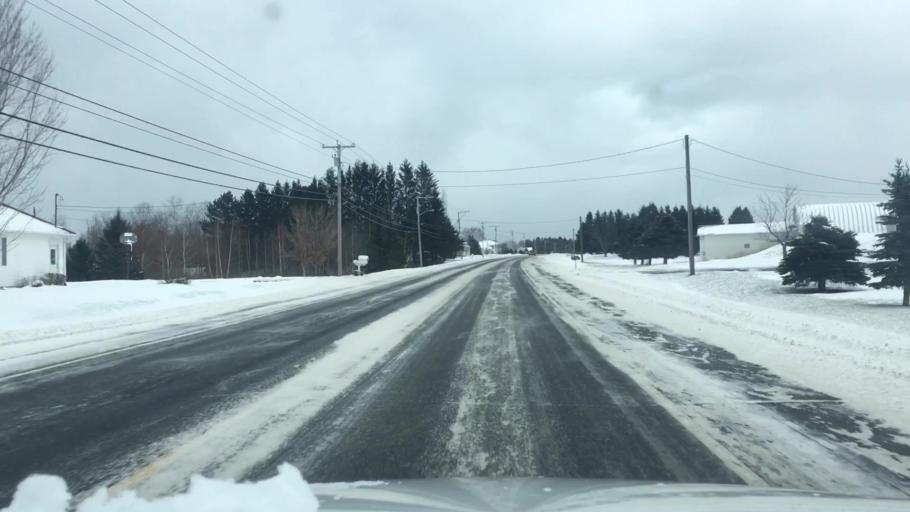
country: US
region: Maine
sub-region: Aroostook County
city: Madawaska
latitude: 47.3447
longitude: -68.2472
